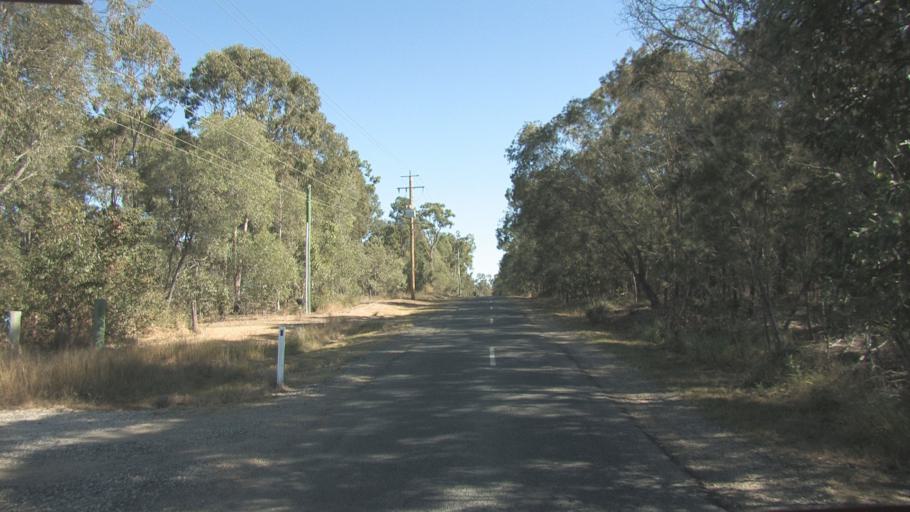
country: AU
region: Queensland
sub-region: Logan
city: North Maclean
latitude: -27.7929
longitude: 153.0546
